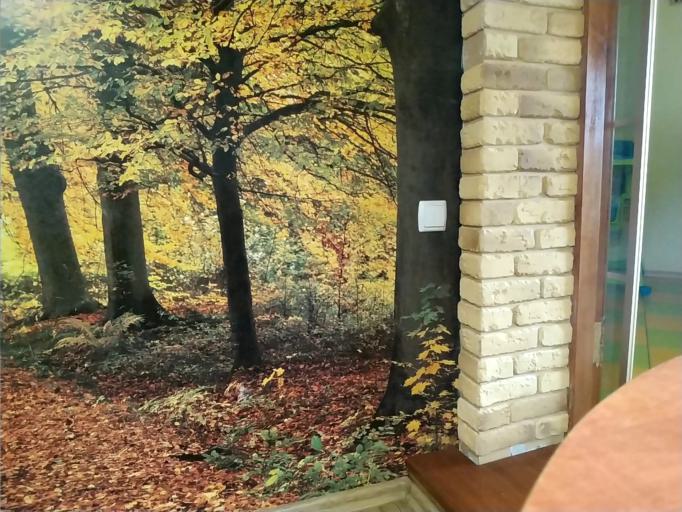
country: RU
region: Smolensk
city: Dorogobuzh
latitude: 54.8850
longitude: 33.3091
